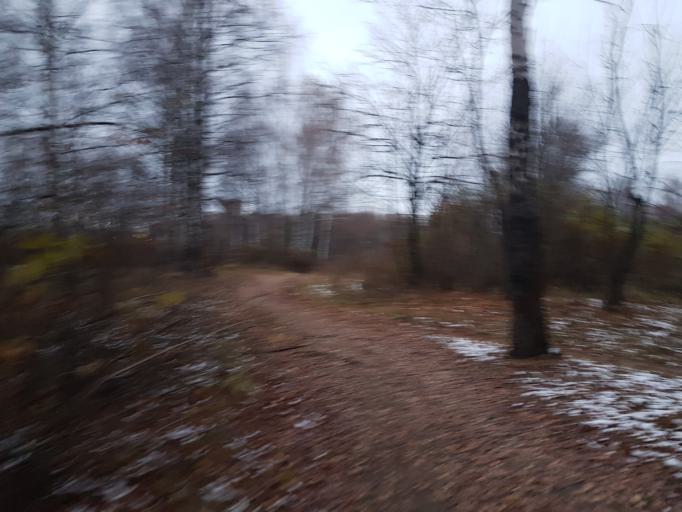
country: RU
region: Moskovskaya
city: Istra
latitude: 55.9027
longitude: 36.8683
